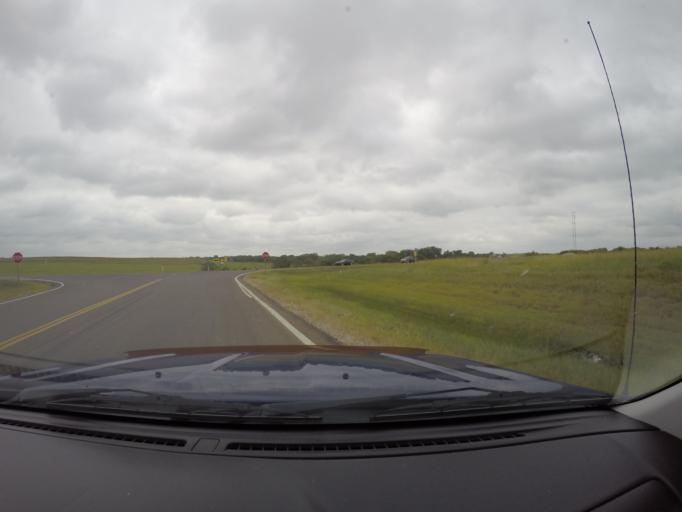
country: US
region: Kansas
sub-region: Morris County
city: Council Grove
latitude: 38.8552
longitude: -96.5012
